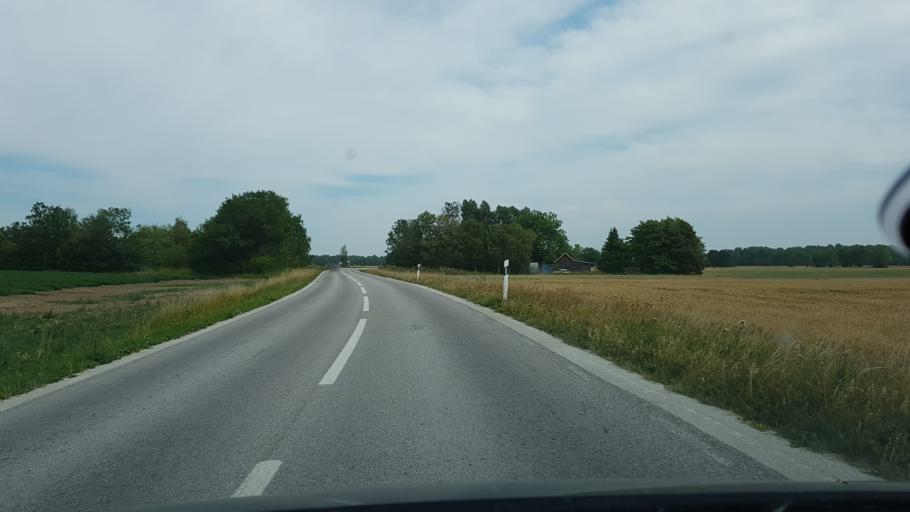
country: SE
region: Gotland
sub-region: Gotland
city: Visby
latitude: 57.7062
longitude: 18.5191
